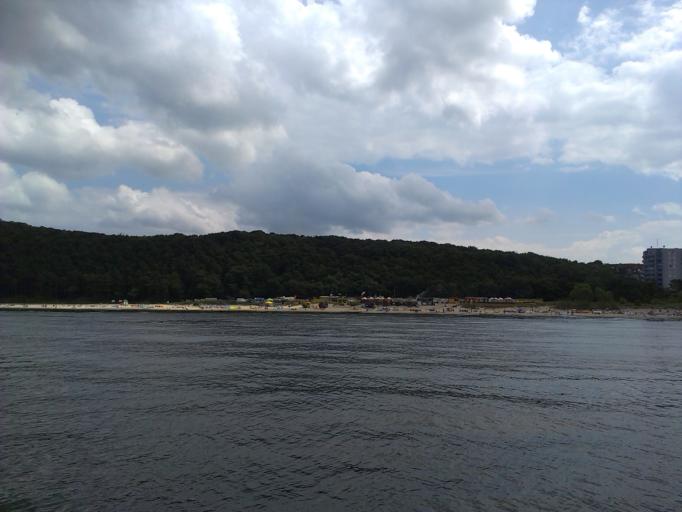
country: PL
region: West Pomeranian Voivodeship
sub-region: Powiat kamienski
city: Miedzyzdroje
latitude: 53.9398
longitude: 14.4556
